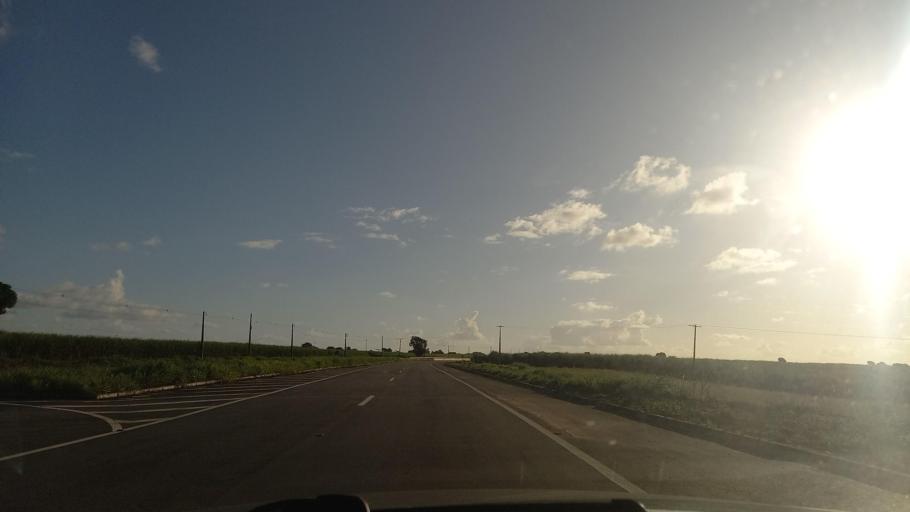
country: BR
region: Alagoas
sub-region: Campo Alegre
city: Campo Alegre
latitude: -9.8231
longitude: -36.2377
